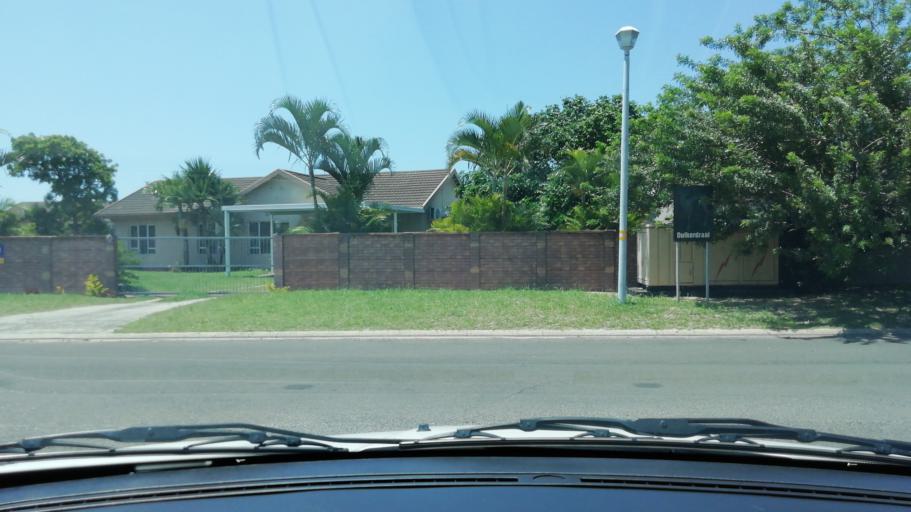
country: ZA
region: KwaZulu-Natal
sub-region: uThungulu District Municipality
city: Richards Bay
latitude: -28.7345
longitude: 32.0524
